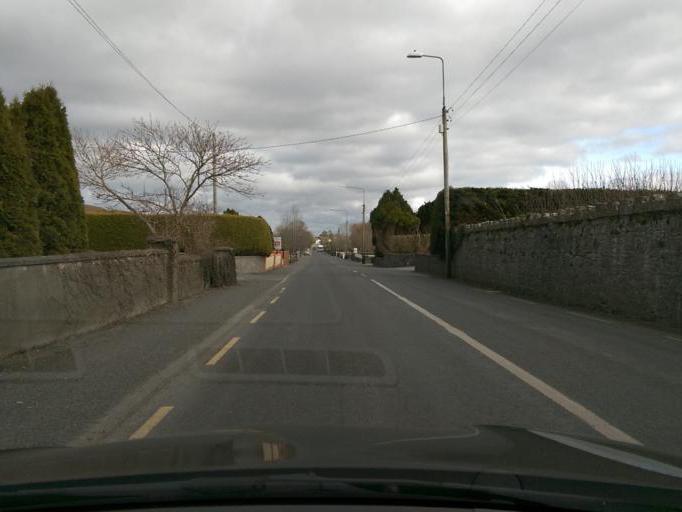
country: IE
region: Connaught
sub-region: County Galway
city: Ballinasloe
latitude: 53.3343
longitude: -8.2515
